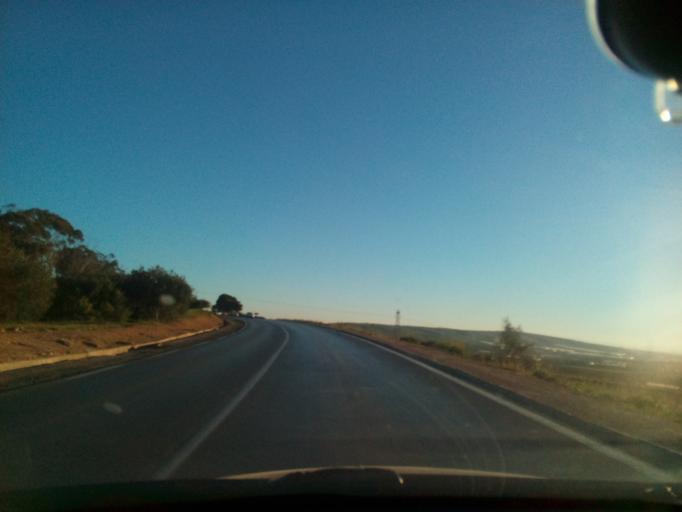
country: DZ
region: Mostaganem
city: Mostaganem
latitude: 35.7651
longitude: 0.2009
